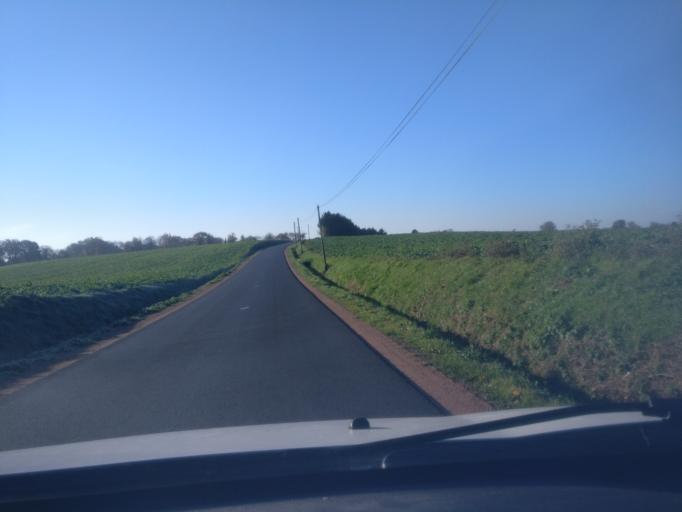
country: FR
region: Brittany
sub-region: Departement d'Ille-et-Vilaine
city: Chavagne
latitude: 48.0146
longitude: -1.7890
